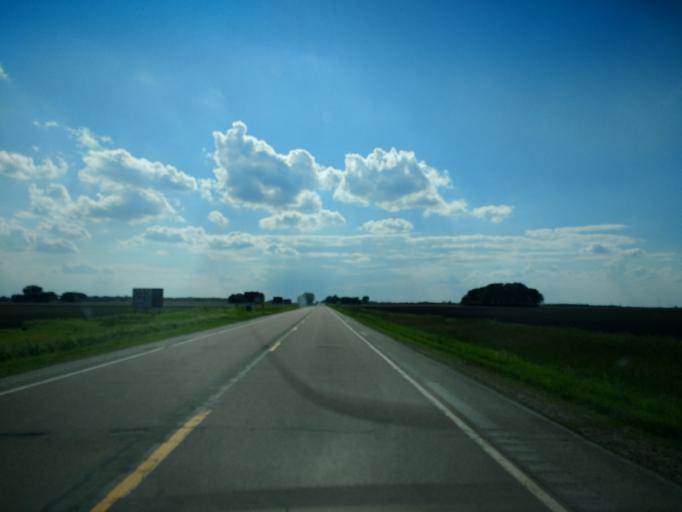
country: US
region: Iowa
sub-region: Clay County
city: Spencer
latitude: 43.1840
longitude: -95.1545
